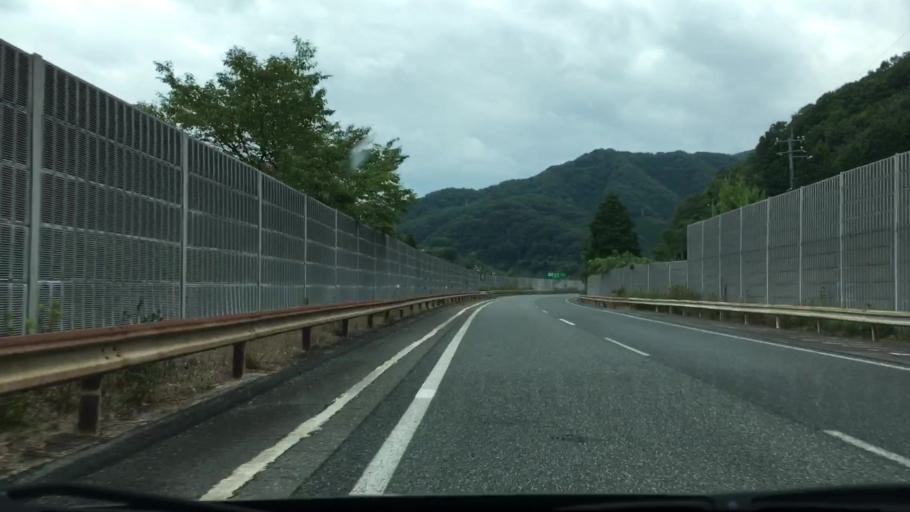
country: JP
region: Okayama
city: Niimi
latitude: 34.9943
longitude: 133.4676
